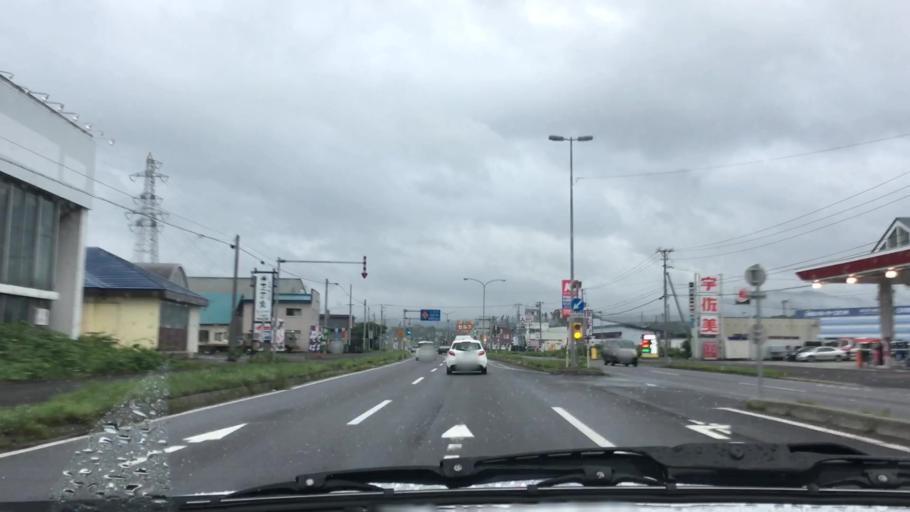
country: JP
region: Hokkaido
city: Nanae
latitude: 42.2507
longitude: 140.2855
